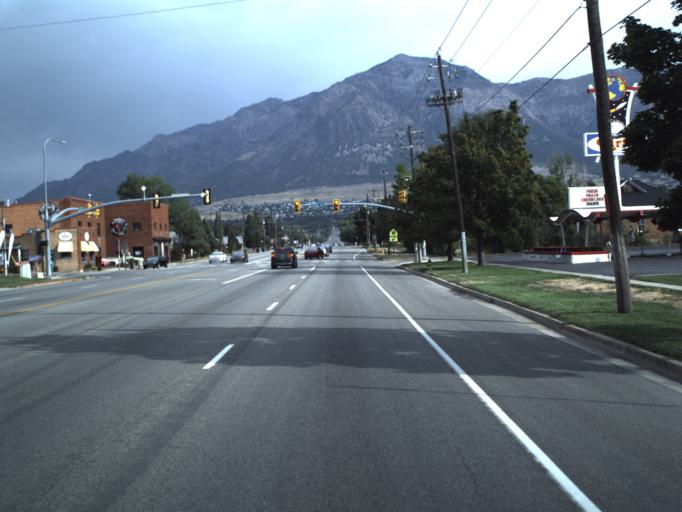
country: US
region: Utah
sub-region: Weber County
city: North Ogden
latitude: 41.2938
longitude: -111.9689
